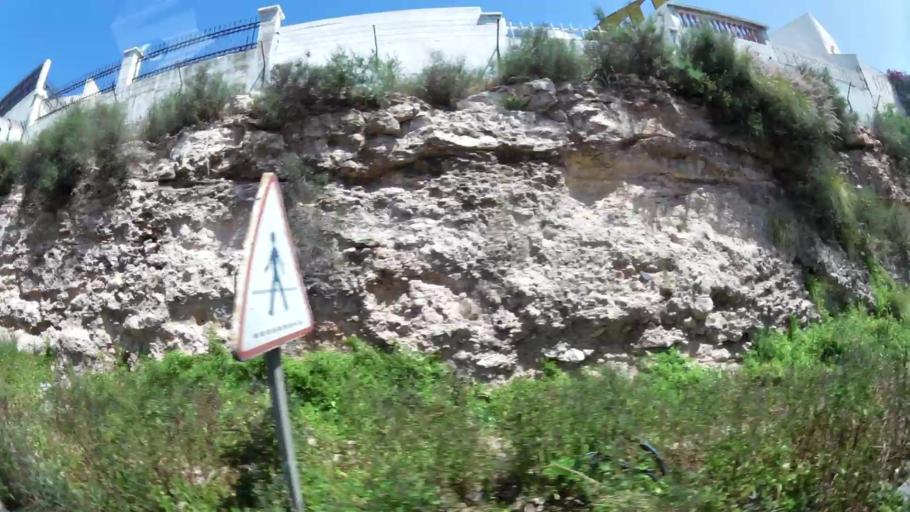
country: MA
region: Souss-Massa-Draa
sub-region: Agadir-Ida-ou-Tnan
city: Agadir
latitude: 30.4361
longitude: -9.5971
